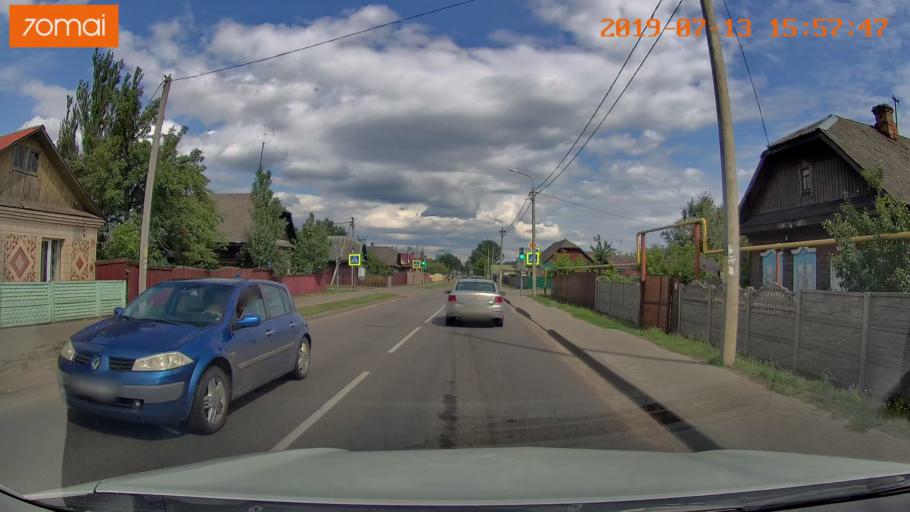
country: BY
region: Mogilev
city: Babruysk
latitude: 53.1464
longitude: 29.2049
